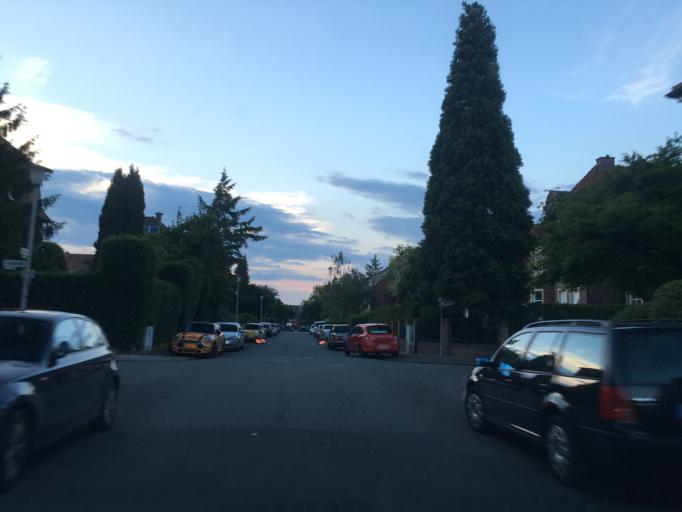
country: DE
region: North Rhine-Westphalia
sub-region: Regierungsbezirk Munster
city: Muenster
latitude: 51.9684
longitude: 7.6594
